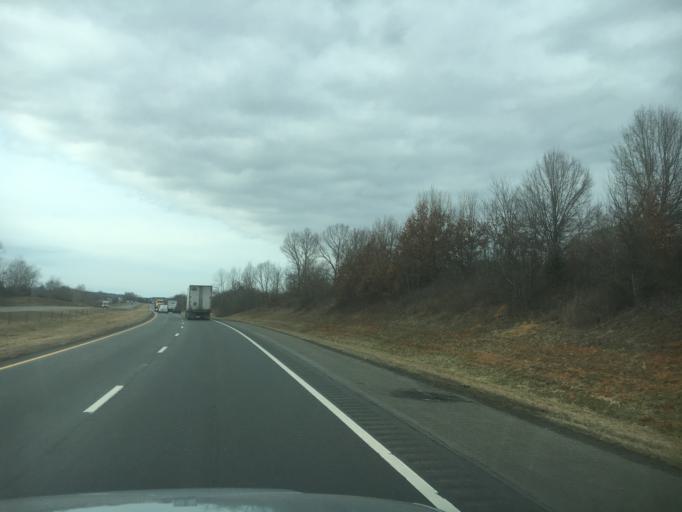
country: US
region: North Carolina
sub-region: Catawba County
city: Maiden
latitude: 35.5399
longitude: -81.2282
